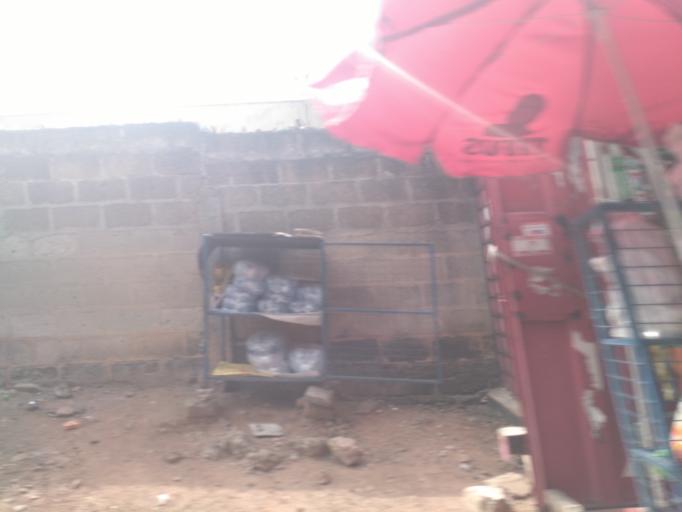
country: GH
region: Ashanti
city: Kumasi
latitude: 6.6753
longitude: -1.6029
